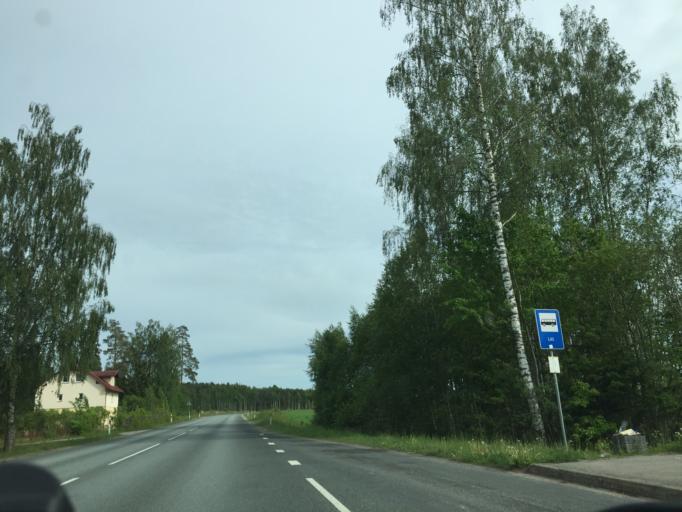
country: LV
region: Beverina
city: Murmuiza
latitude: 57.4670
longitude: 25.4113
